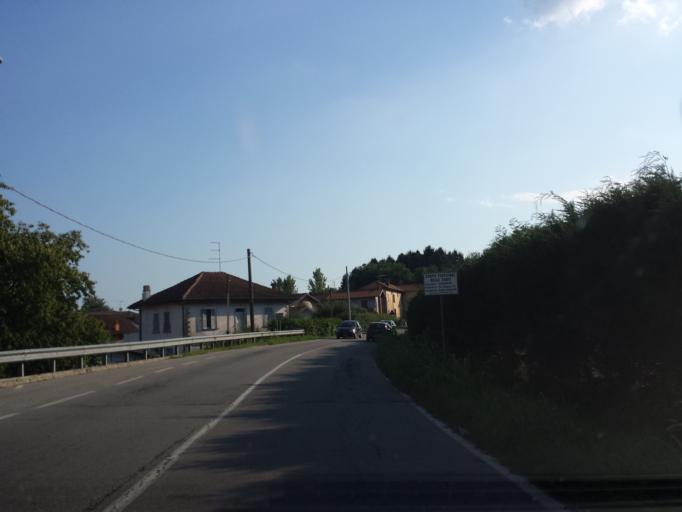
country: IT
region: Lombardy
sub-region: Provincia di Varese
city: Angera
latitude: 45.7857
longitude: 8.5939
